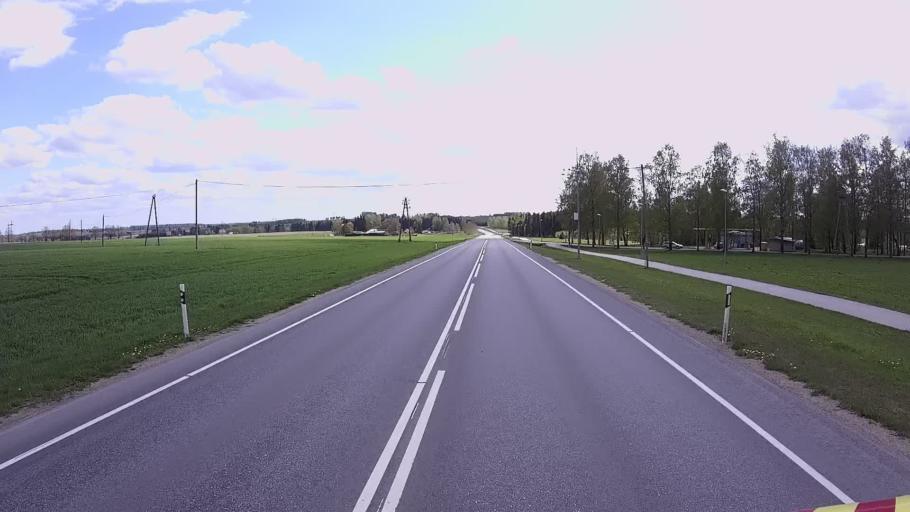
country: EE
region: Jogevamaa
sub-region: Tabivere vald
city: Tabivere
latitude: 58.4920
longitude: 26.6833
